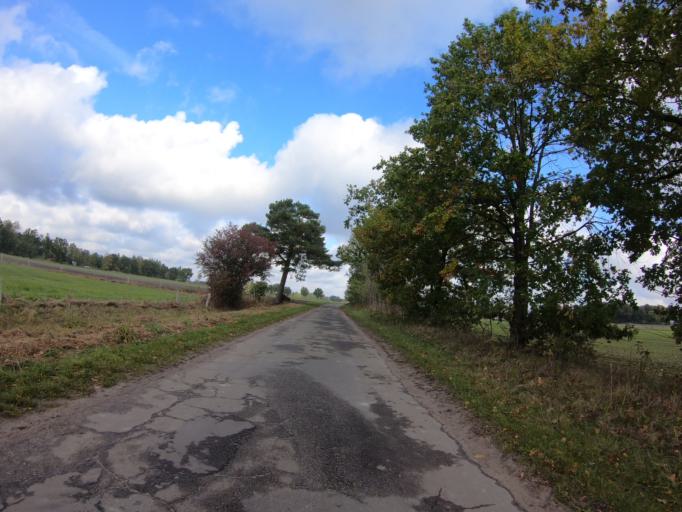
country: DE
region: Lower Saxony
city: Wagenhoff
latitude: 52.5281
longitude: 10.5374
